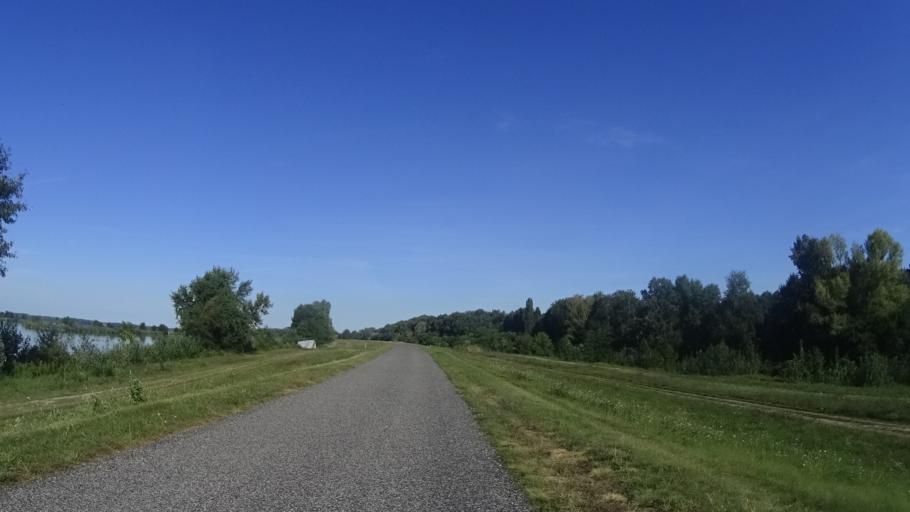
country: SK
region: Bratislavsky
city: Dunajska Luzna
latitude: 48.0557
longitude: 17.2298
